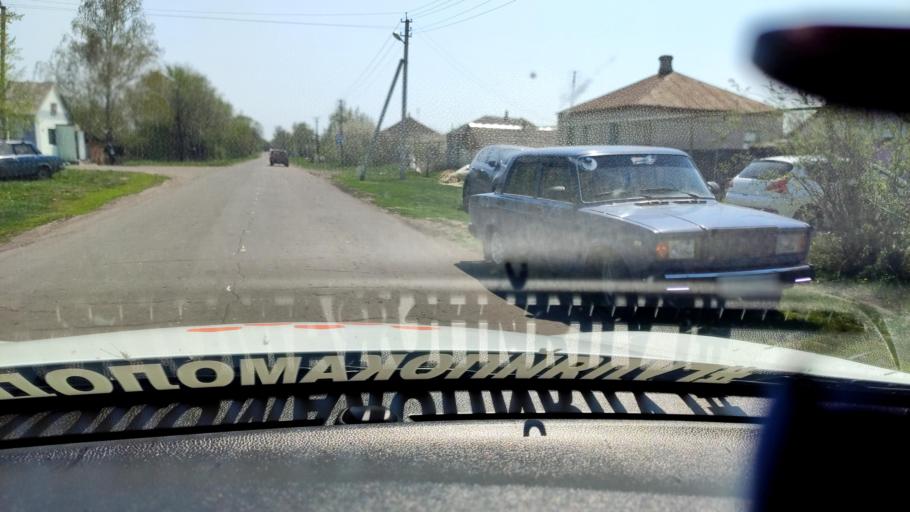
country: RU
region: Voronezj
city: Uryv-Pokrovka
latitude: 51.0801
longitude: 39.1135
